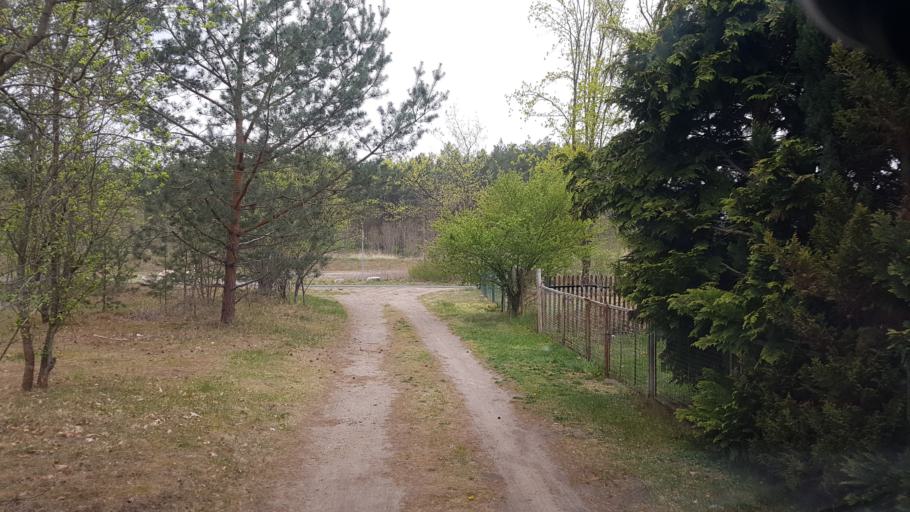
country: DE
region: Brandenburg
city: Altdobern
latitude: 51.6442
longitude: 14.0179
